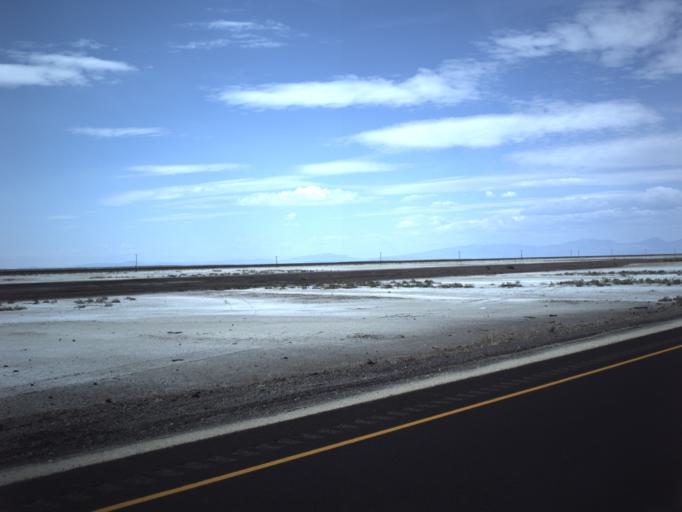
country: US
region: Utah
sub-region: Tooele County
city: Wendover
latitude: 40.7319
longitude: -113.5042
